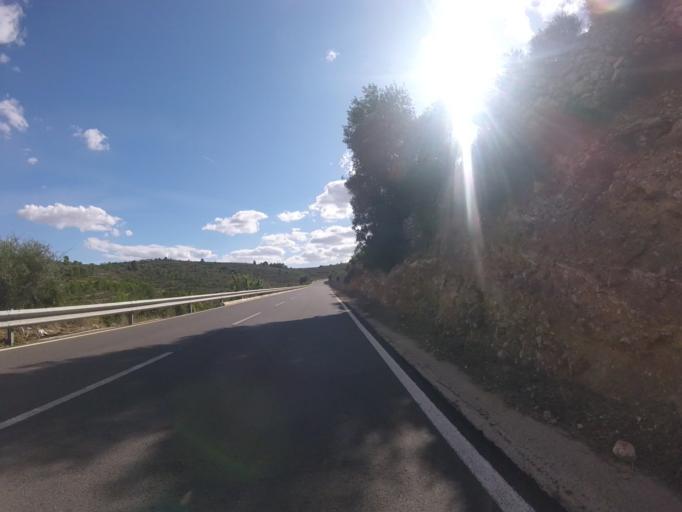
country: ES
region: Valencia
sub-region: Provincia de Castello
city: Cuevas de Vinroma
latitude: 40.3190
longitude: 0.1339
